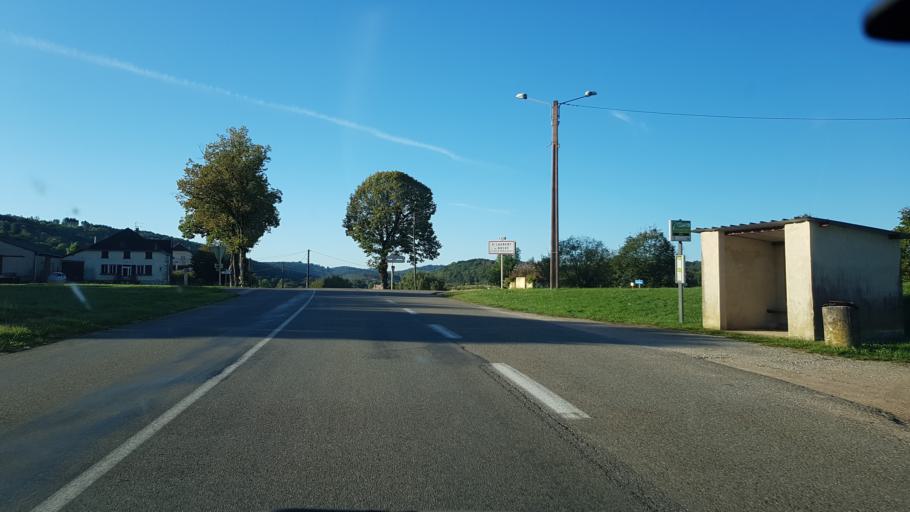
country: FR
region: Franche-Comte
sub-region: Departement du Jura
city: Lons-le-Saunier
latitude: 46.5998
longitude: 5.5198
